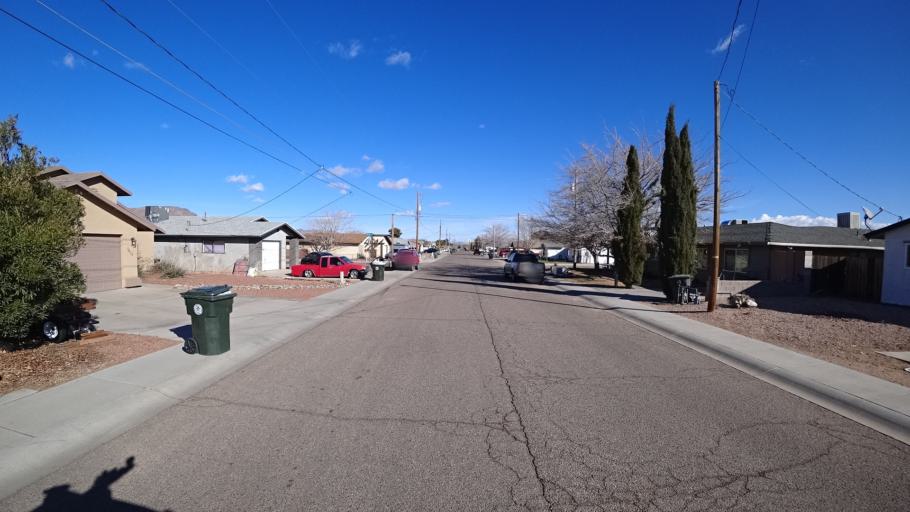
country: US
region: Arizona
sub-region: Mohave County
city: New Kingman-Butler
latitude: 35.2281
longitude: -114.0183
